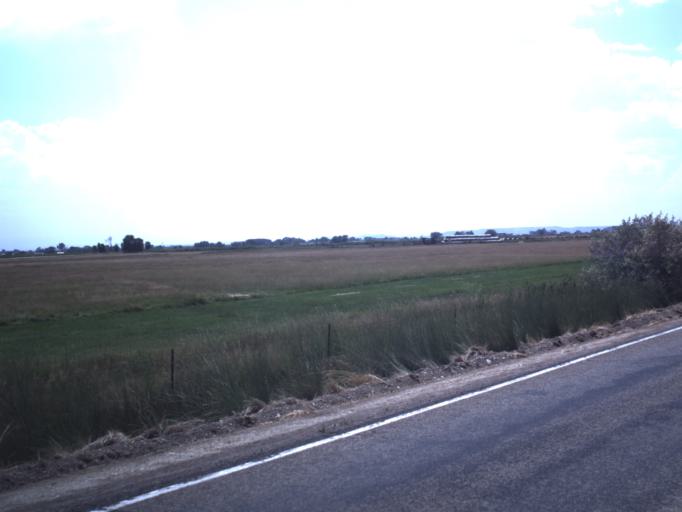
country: US
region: Utah
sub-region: Duchesne County
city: Roosevelt
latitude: 40.4329
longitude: -109.9594
